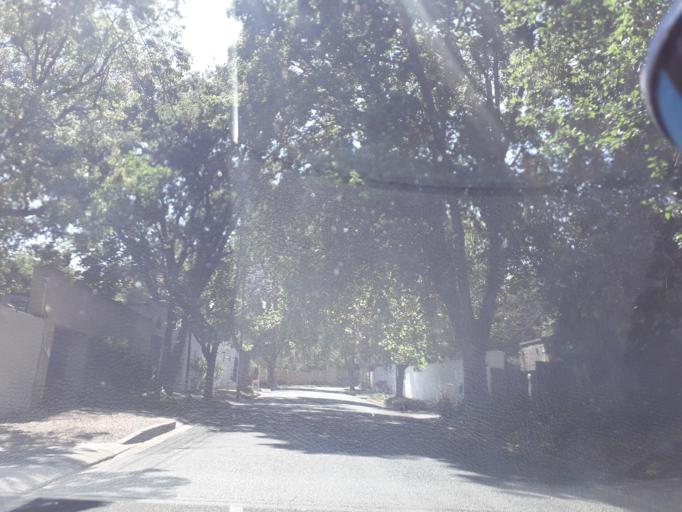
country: ZA
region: Gauteng
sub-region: City of Johannesburg Metropolitan Municipality
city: Johannesburg
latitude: -26.1433
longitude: 28.0310
